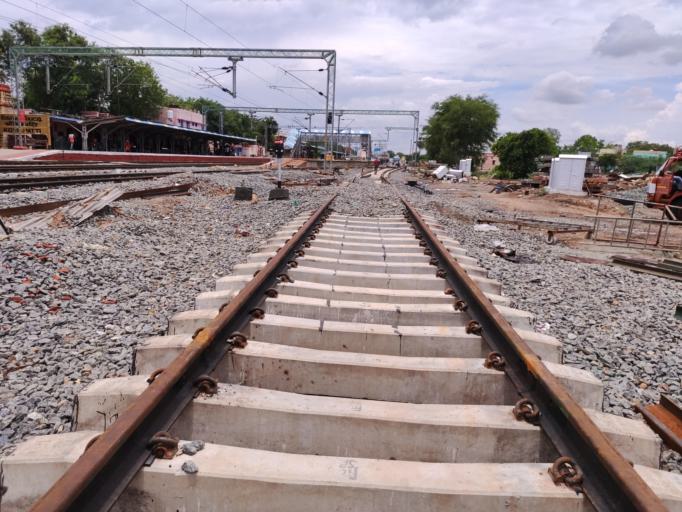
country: IN
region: Tamil Nadu
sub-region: Thoothukkudi
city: Kovilpatti
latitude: 9.1838
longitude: 77.8743
